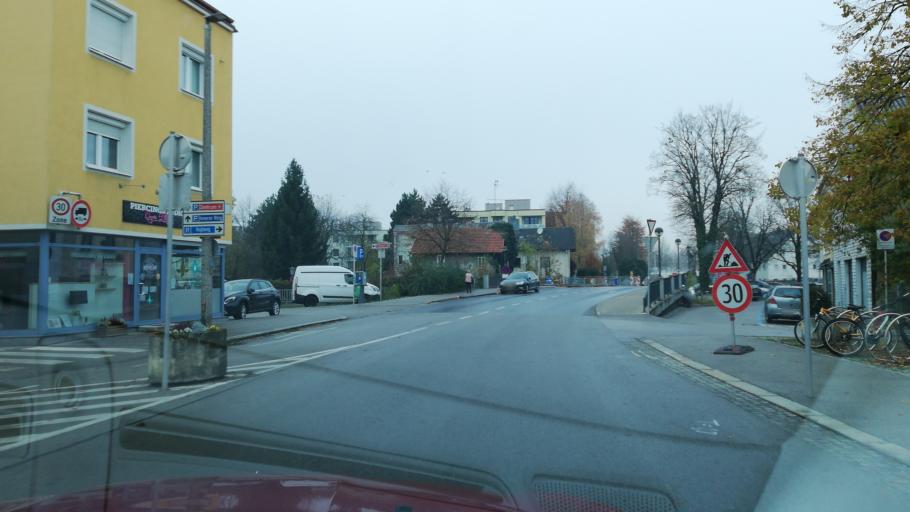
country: AT
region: Upper Austria
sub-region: Politischer Bezirk Ried im Innkreis
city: Ried im Innkreis
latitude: 48.2111
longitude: 13.4879
